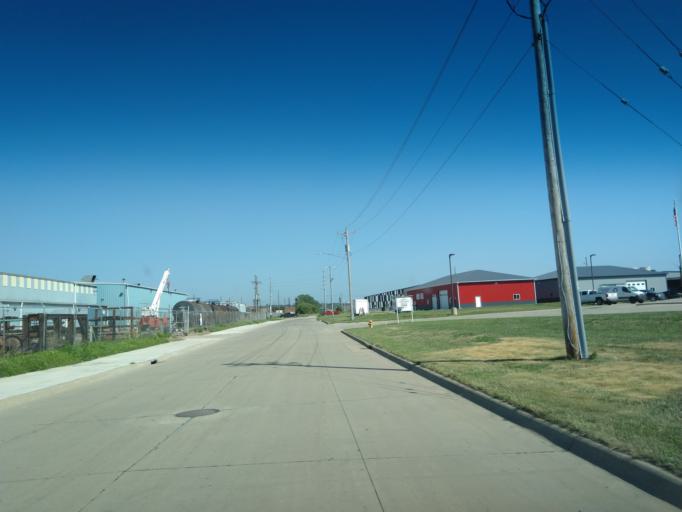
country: US
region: Iowa
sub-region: Woodbury County
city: Sioux City
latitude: 42.4812
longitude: -96.3857
